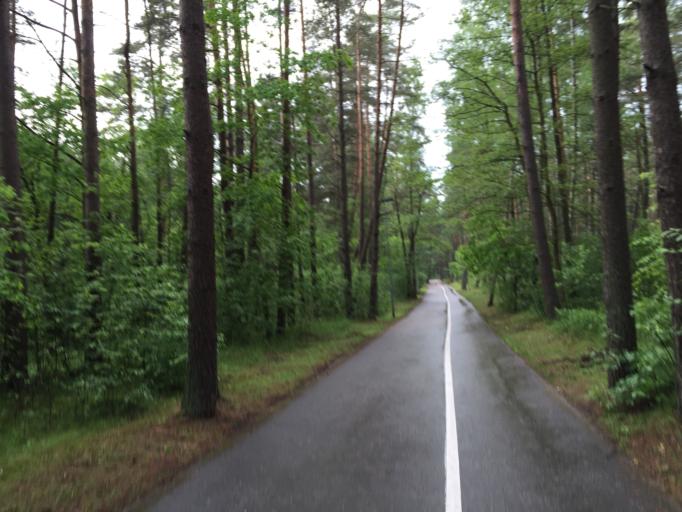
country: LT
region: Klaipedos apskritis
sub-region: Klaipeda
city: Klaipeda
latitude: 55.7500
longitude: 21.1185
